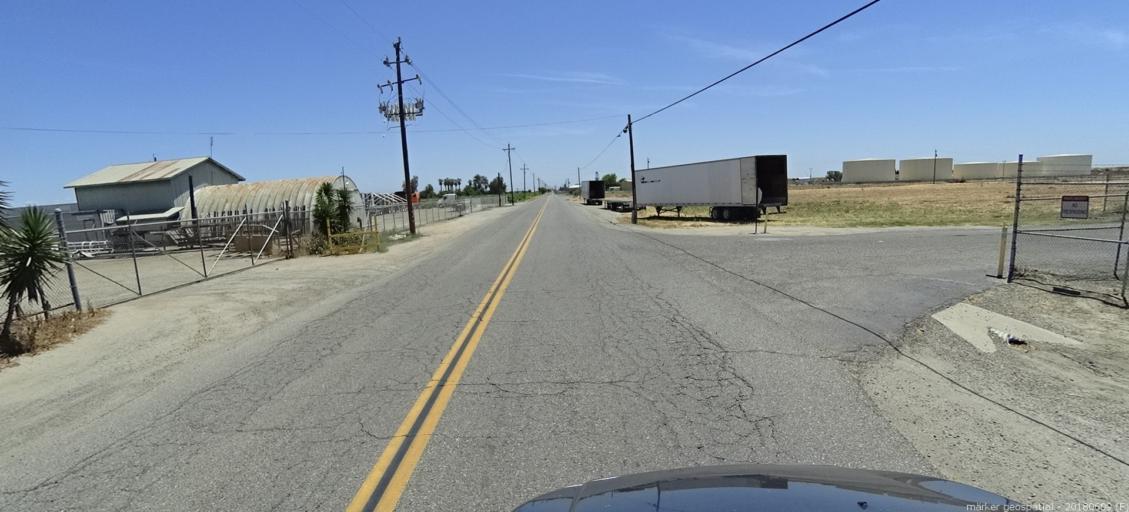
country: US
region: California
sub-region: Madera County
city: Madera
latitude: 36.9383
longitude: -120.1005
